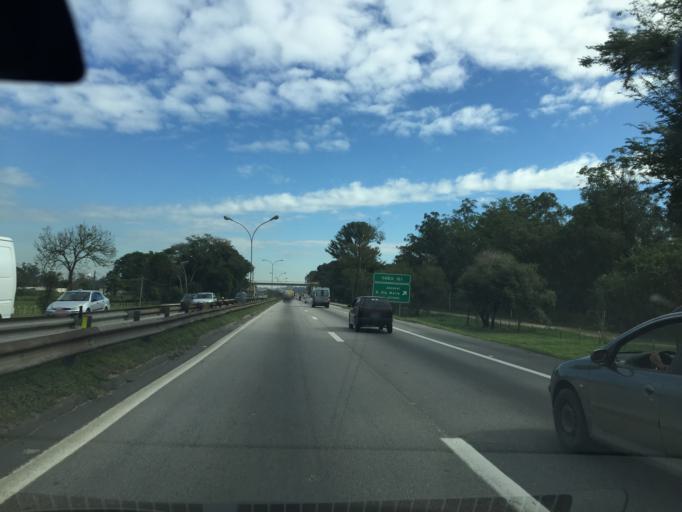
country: BR
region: Sao Paulo
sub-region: Jacarei
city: Jacarei
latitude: -23.2729
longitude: -45.9710
